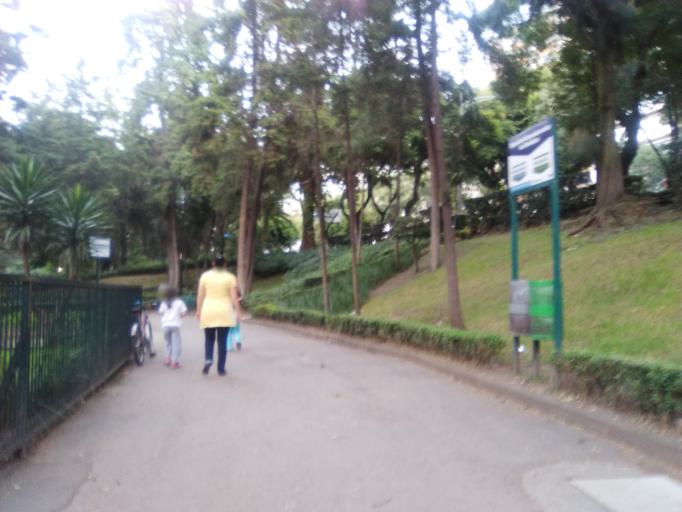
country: MX
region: Mexico City
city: Colonia del Valle
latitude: 19.3771
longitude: -99.1782
